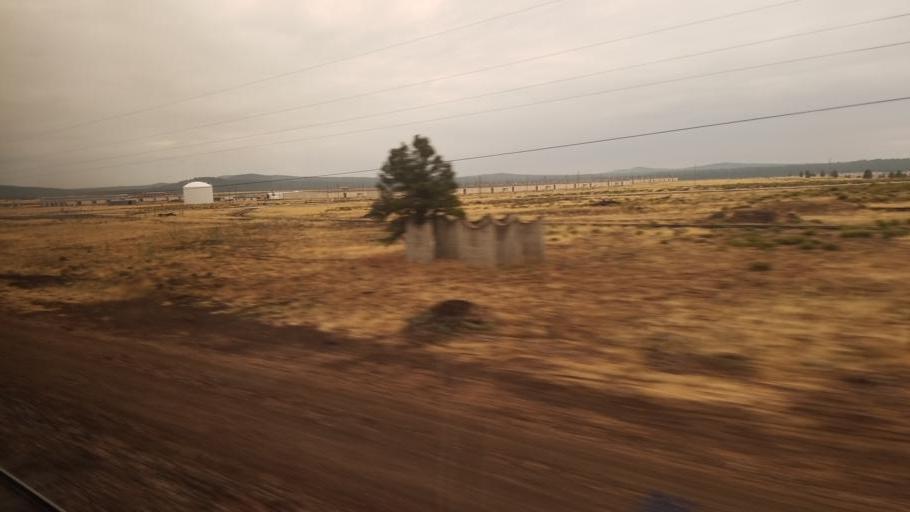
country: US
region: Arizona
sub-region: Coconino County
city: Parks
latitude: 35.2388
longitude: -111.8445
